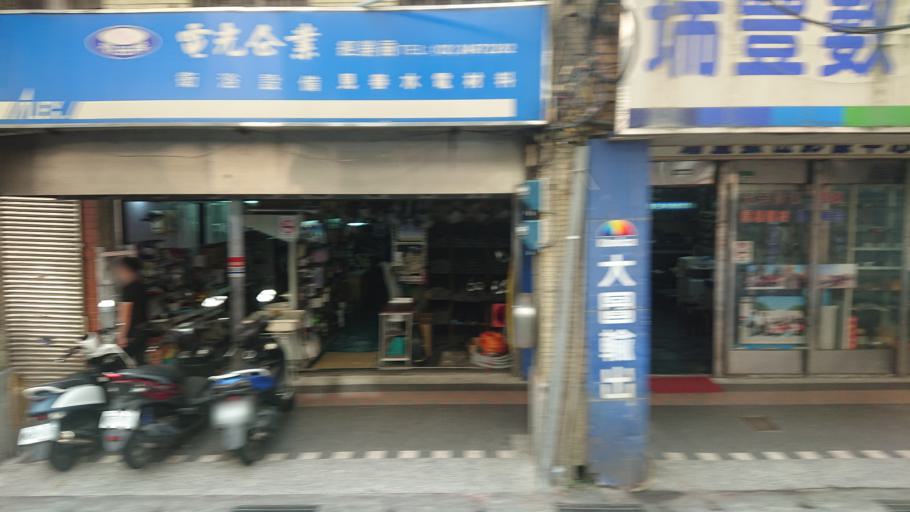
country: TW
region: Taiwan
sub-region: Keelung
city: Keelung
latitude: 25.1078
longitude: 121.8074
